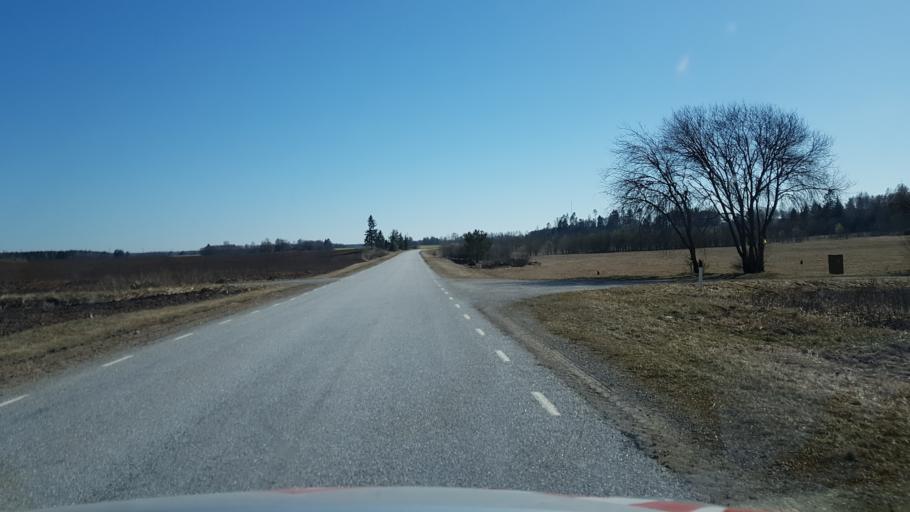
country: EE
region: Jaervamaa
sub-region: Koeru vald
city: Koeru
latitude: 59.0338
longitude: 26.0909
